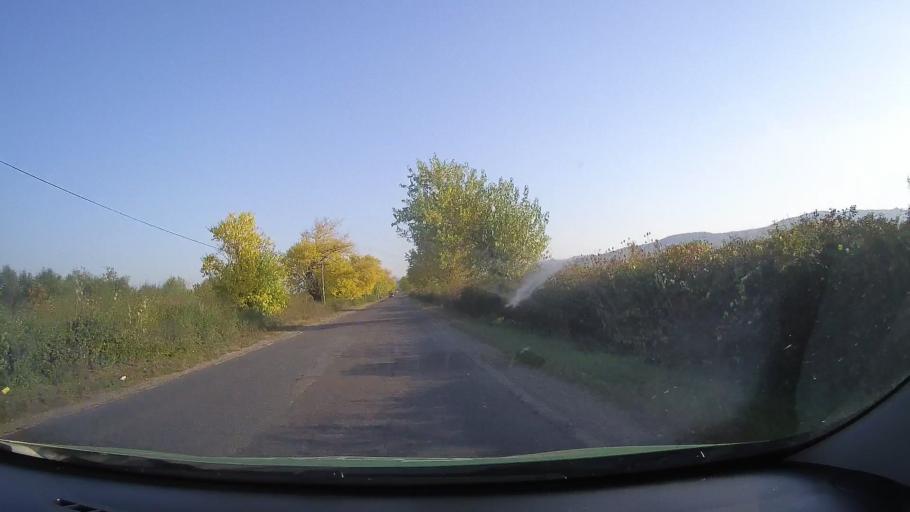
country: RO
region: Arad
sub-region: Comuna Pancota
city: Maderat
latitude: 46.3116
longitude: 21.7037
